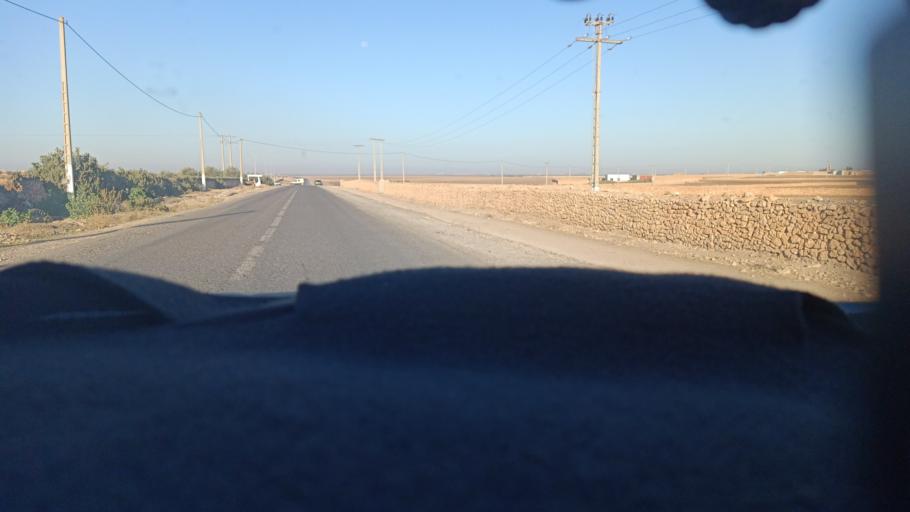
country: MA
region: Doukkala-Abda
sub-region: Safi
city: Youssoufia
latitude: 32.3709
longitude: -8.6790
